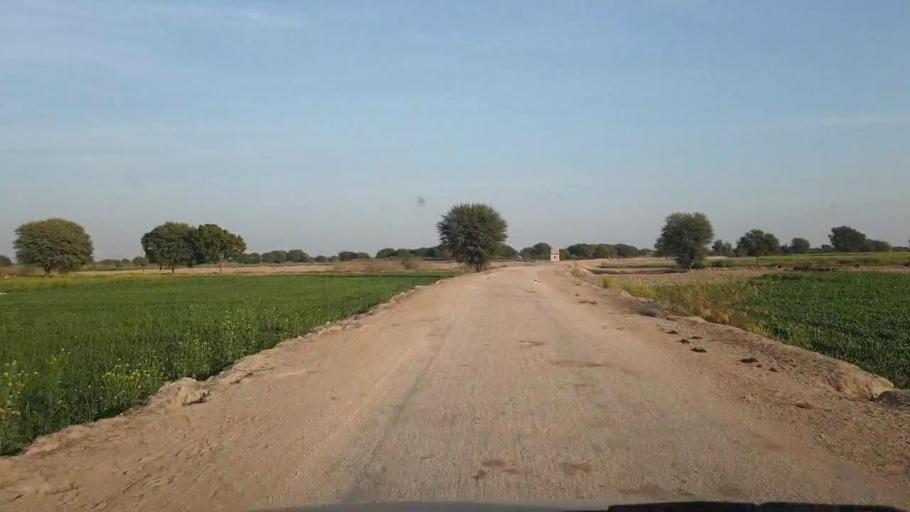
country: PK
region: Sindh
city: Chambar
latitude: 25.2603
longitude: 68.8004
